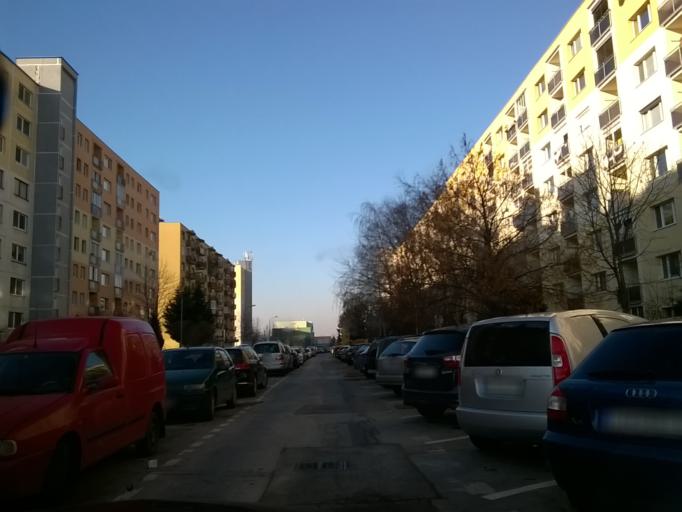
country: SK
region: Nitriansky
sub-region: Okres Nitra
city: Nitra
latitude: 48.3030
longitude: 18.0501
